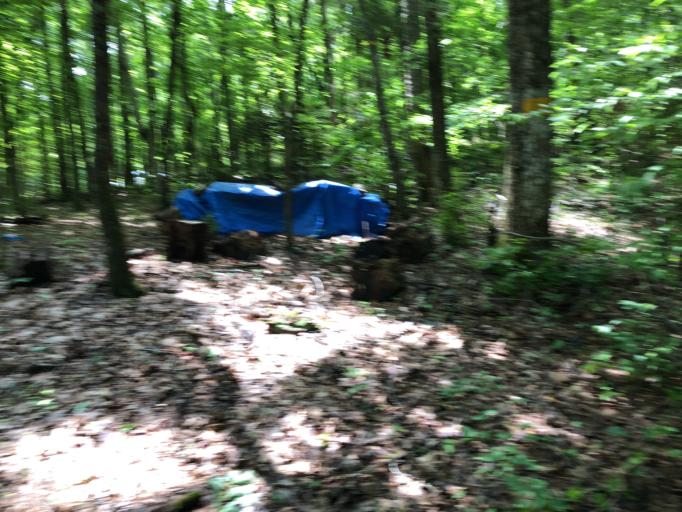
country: US
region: Alabama
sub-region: Chambers County
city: Valley
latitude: 32.6905
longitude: -85.1871
